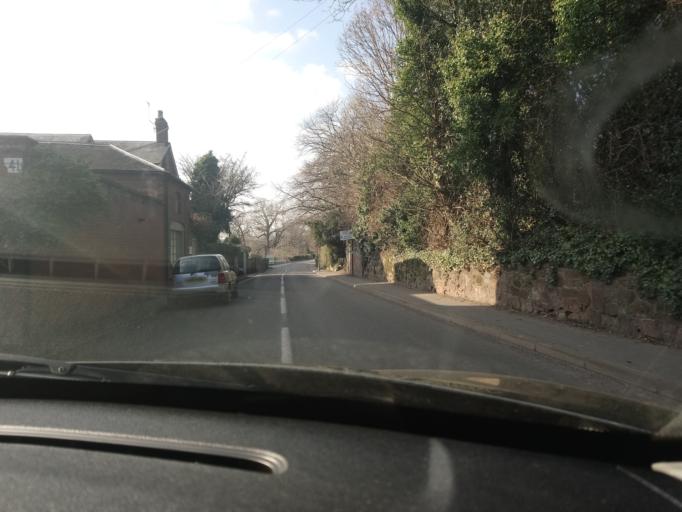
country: GB
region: England
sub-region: Shropshire
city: Shrewsbury
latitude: 52.7164
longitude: -2.7568
